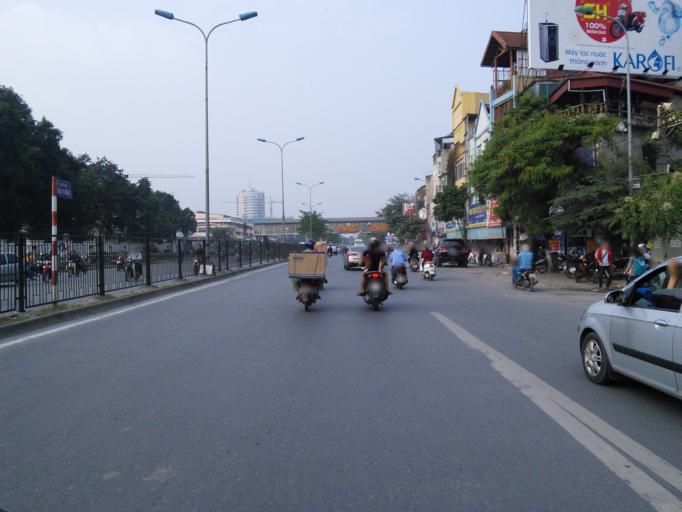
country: VN
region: Ha Noi
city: Hai BaTrung
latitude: 21.0003
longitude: 105.8414
